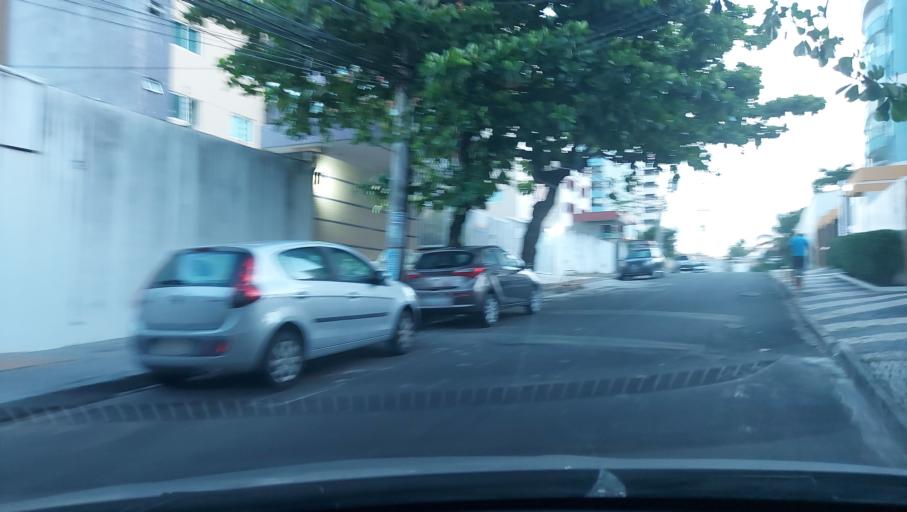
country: BR
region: Bahia
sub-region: Salvador
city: Salvador
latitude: -12.9873
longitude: -38.4389
